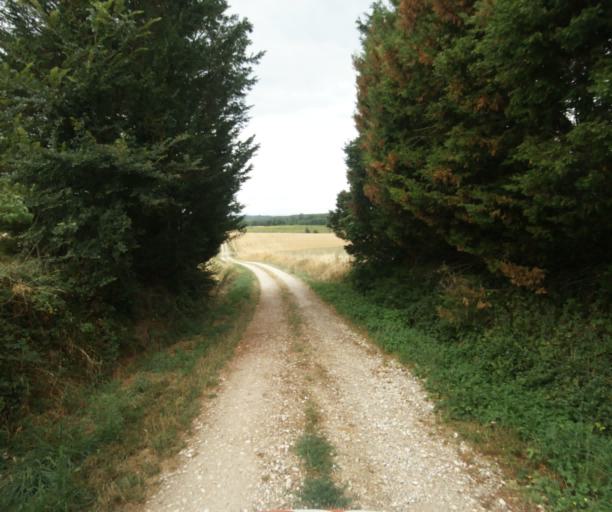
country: FR
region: Midi-Pyrenees
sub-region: Departement de la Haute-Garonne
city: Revel
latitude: 43.4351
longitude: 1.9597
